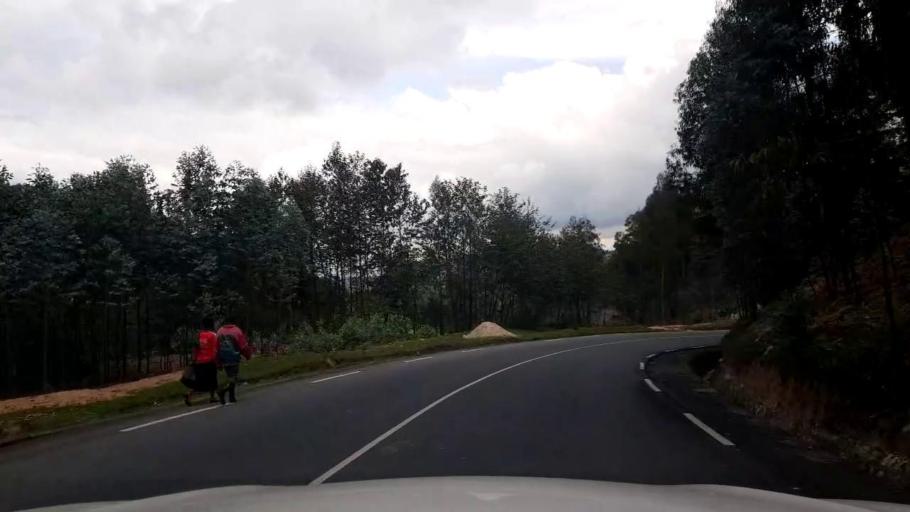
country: RW
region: Northern Province
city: Musanze
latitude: -1.6800
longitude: 29.5163
